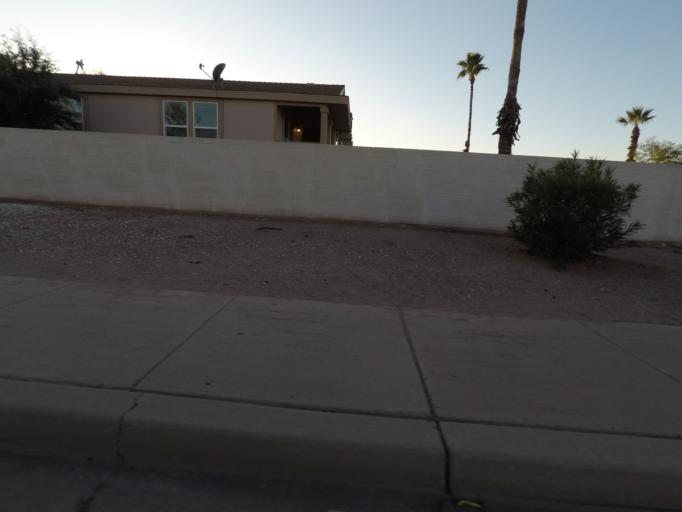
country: US
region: Arizona
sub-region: Maricopa County
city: Guadalupe
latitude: 33.3822
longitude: -111.9438
